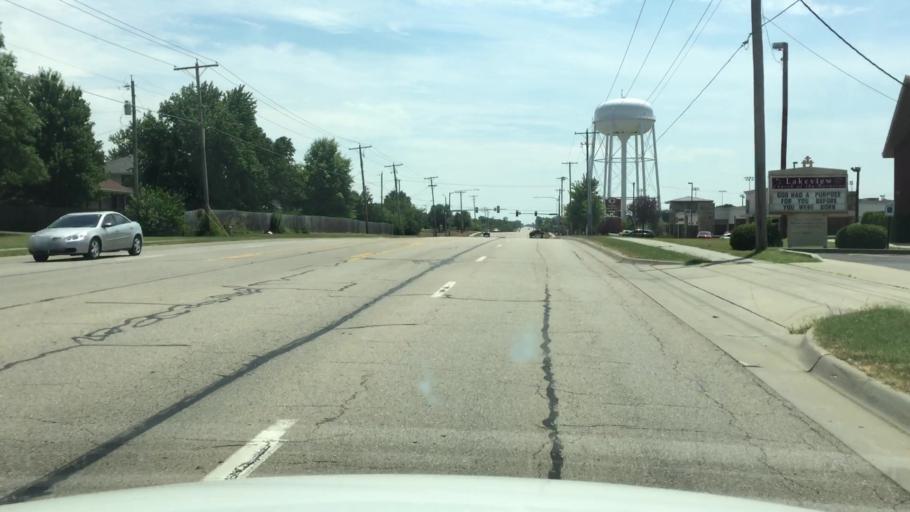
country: US
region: Kansas
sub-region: Shawnee County
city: Topeka
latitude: 39.0171
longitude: -95.6143
